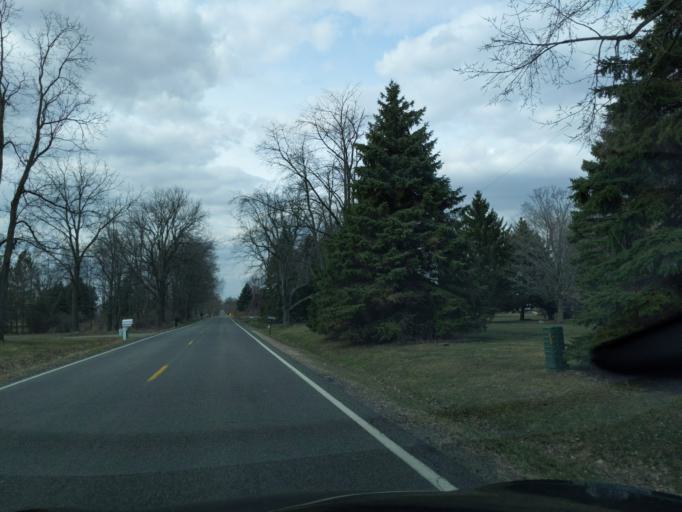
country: US
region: Michigan
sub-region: Ingham County
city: Mason
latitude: 42.5336
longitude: -84.4830
